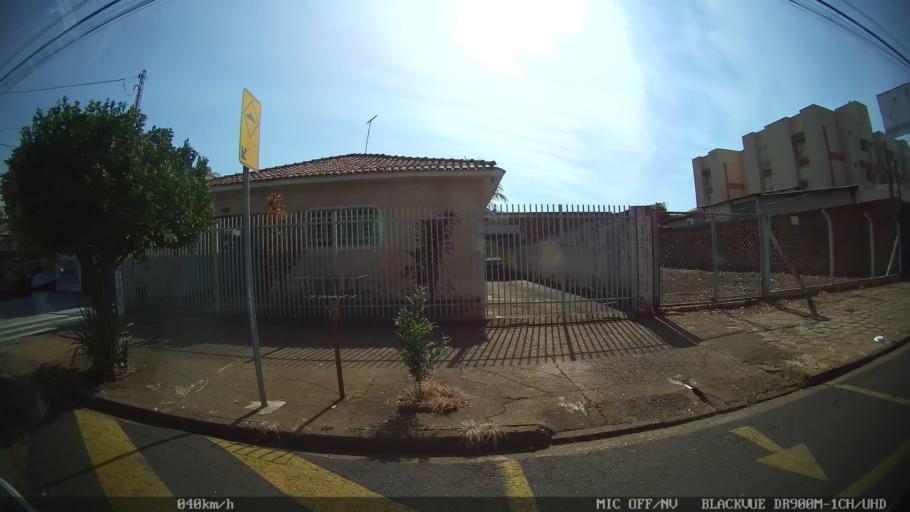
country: BR
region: Sao Paulo
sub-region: Sao Jose Do Rio Preto
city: Sao Jose do Rio Preto
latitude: -20.7962
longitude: -49.4099
